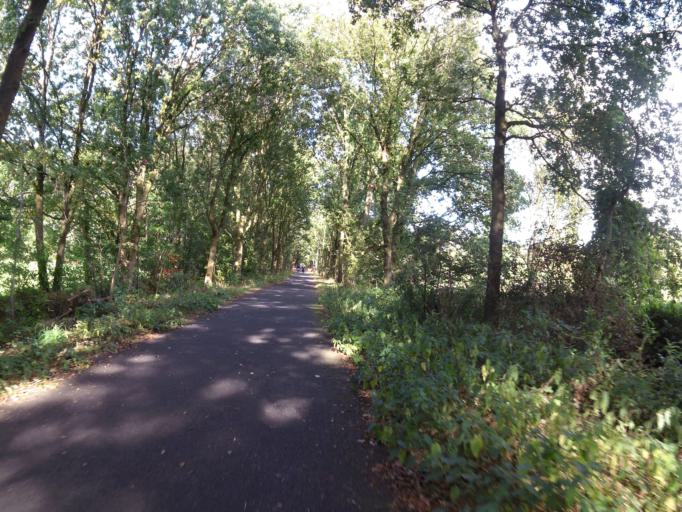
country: NL
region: North Brabant
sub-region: Gemeente Heeze-Leende
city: Heeze
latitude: 51.3774
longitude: 5.5452
